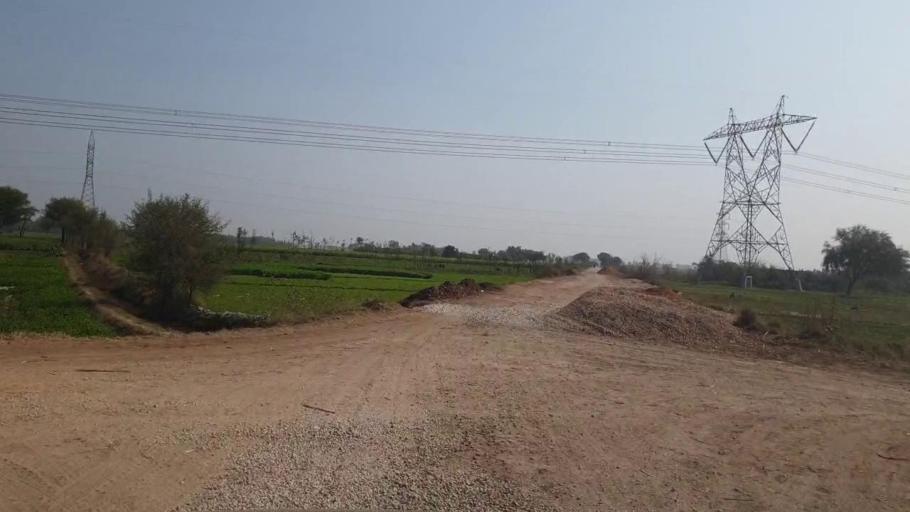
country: PK
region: Sindh
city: Bhit Shah
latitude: 25.7226
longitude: 68.5391
